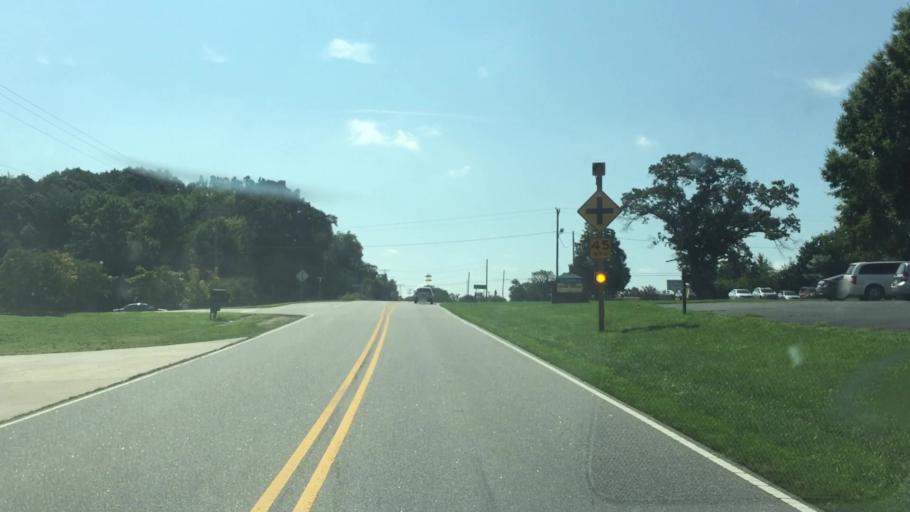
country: US
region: North Carolina
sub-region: Stanly County
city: Oakboro
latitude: 35.1321
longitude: -80.3707
